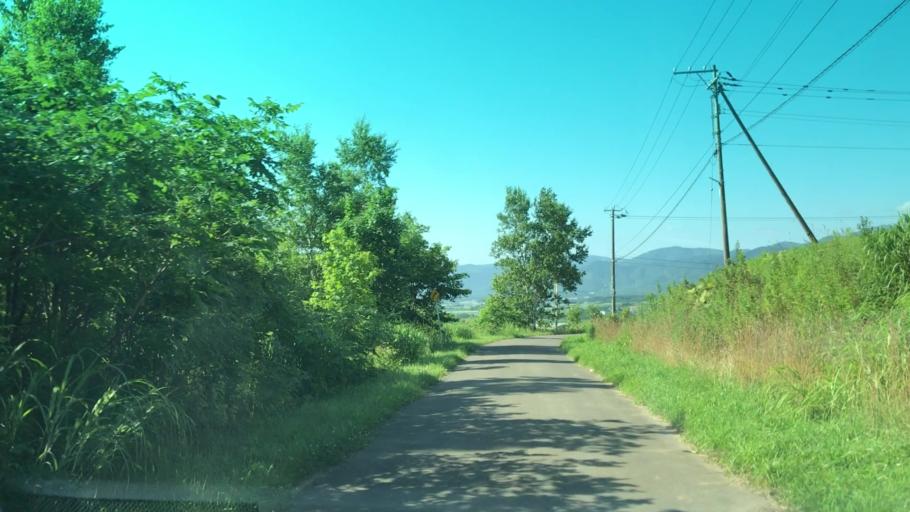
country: JP
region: Hokkaido
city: Iwanai
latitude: 42.9720
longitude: 140.6098
